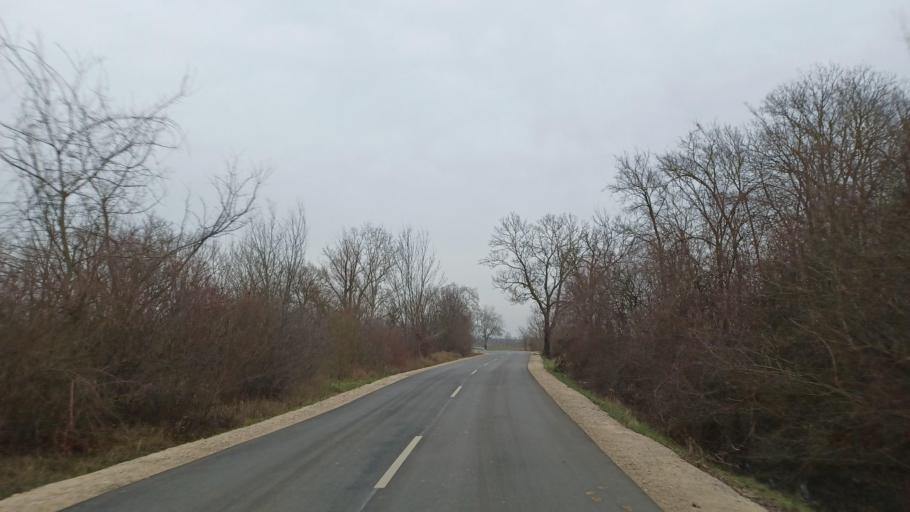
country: HU
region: Tolna
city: Nagydorog
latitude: 46.5618
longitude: 18.5992
